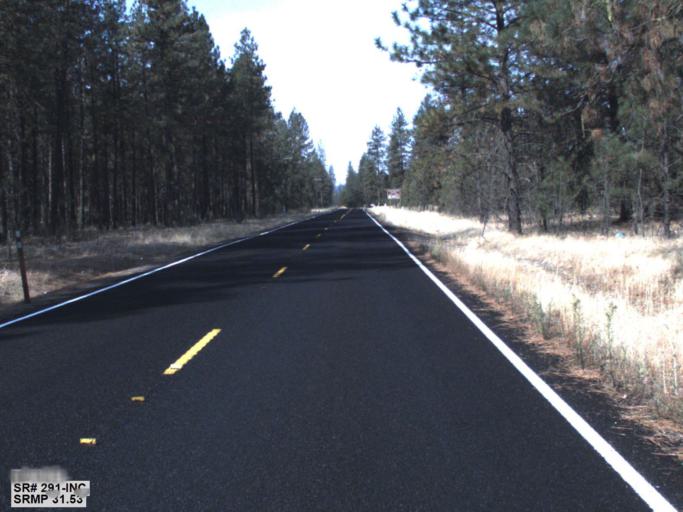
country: US
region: Washington
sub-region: Spokane County
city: Fairchild Air Force Base
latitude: 47.8394
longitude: -117.8283
